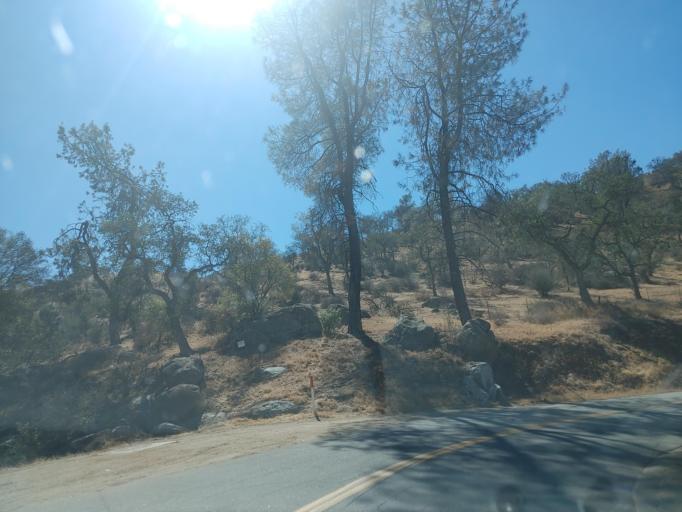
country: US
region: California
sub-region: Kern County
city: Golden Hills
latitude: 35.1935
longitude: -118.5357
